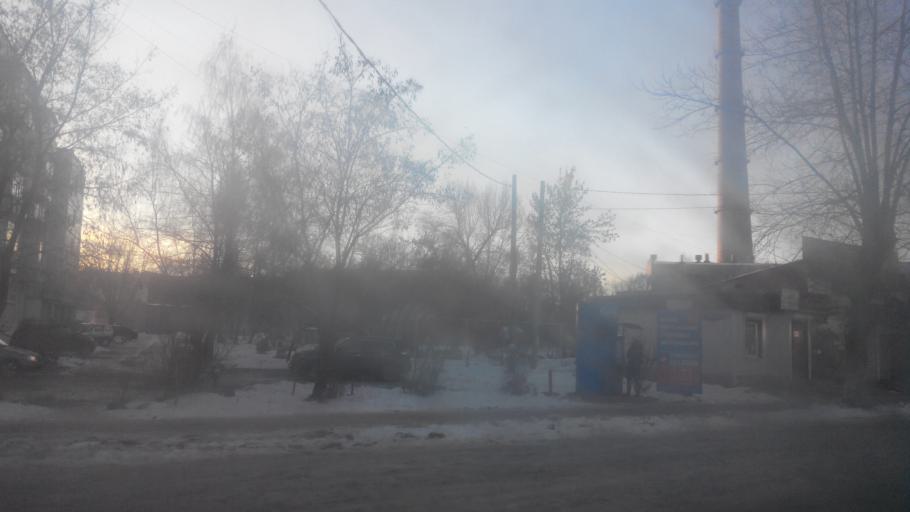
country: RU
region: Tula
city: Uzlovaya
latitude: 53.9708
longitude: 38.1741
